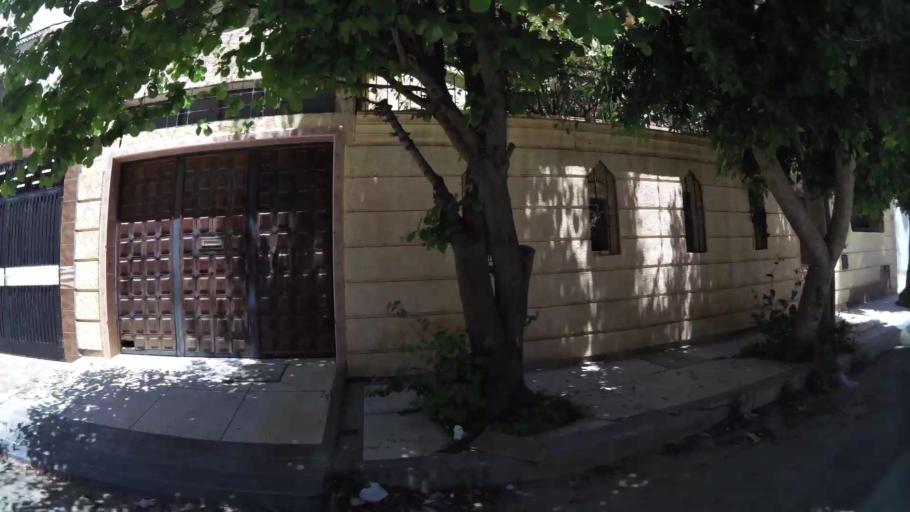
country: MA
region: Oriental
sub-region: Oujda-Angad
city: Oujda
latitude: 34.6636
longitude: -1.9210
